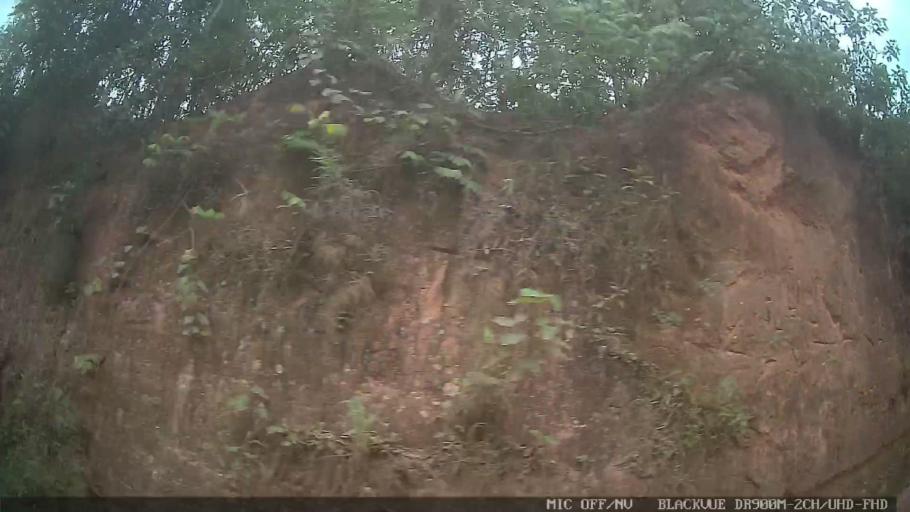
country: BR
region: Sao Paulo
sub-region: Bom Jesus Dos Perdoes
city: Bom Jesus dos Perdoes
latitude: -23.1712
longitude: -46.5132
